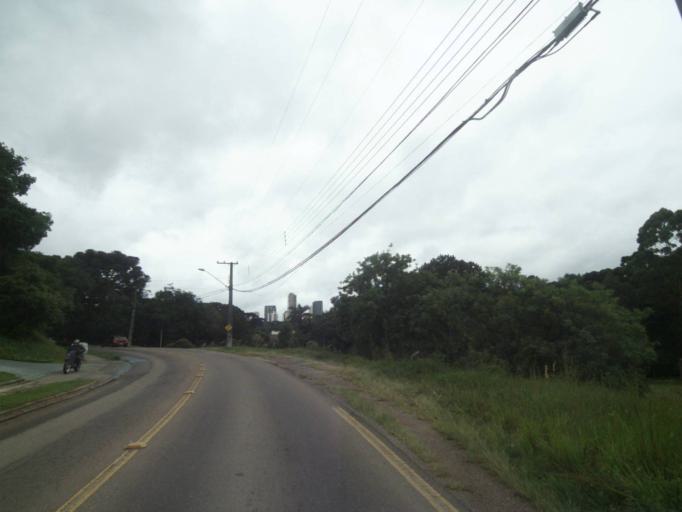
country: BR
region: Parana
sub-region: Curitiba
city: Curitiba
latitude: -25.4495
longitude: -49.3301
